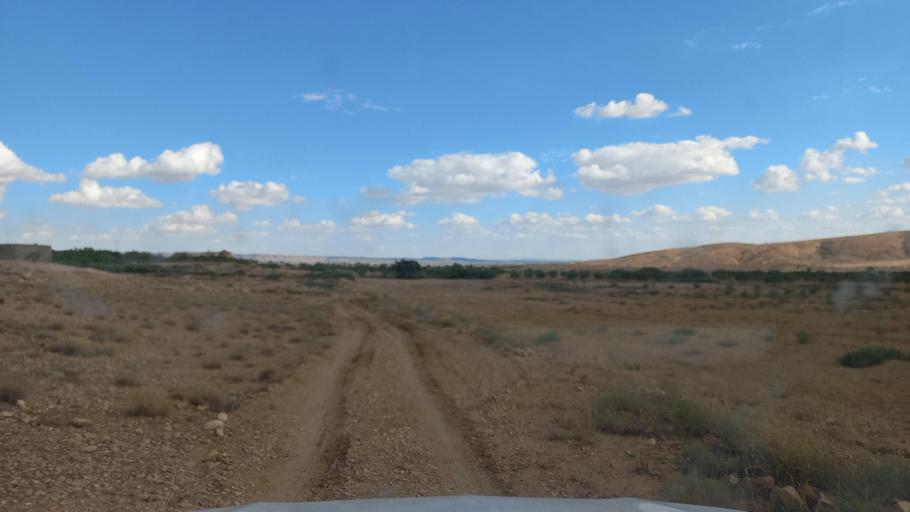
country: TN
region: Al Qasrayn
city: Sbiba
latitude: 35.4030
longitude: 9.0116
